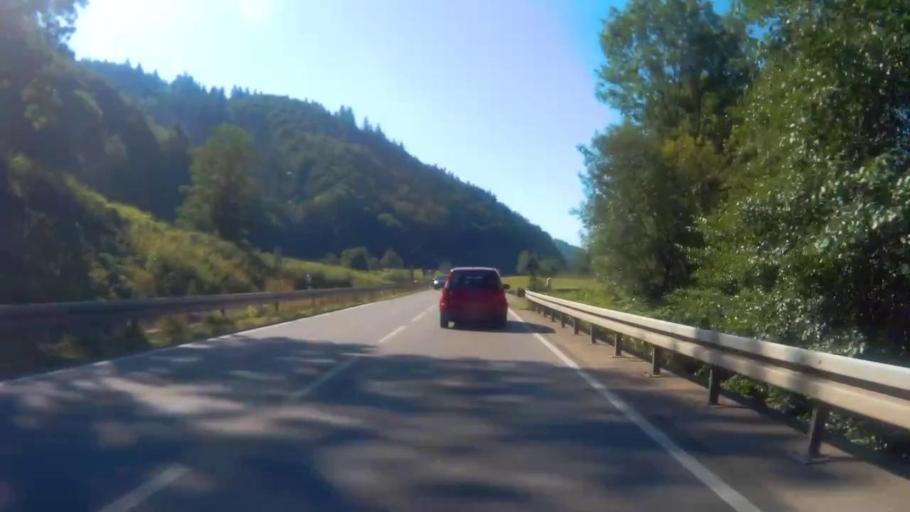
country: DE
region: Baden-Wuerttemberg
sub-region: Freiburg Region
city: Hausen
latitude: 47.6904
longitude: 7.8441
